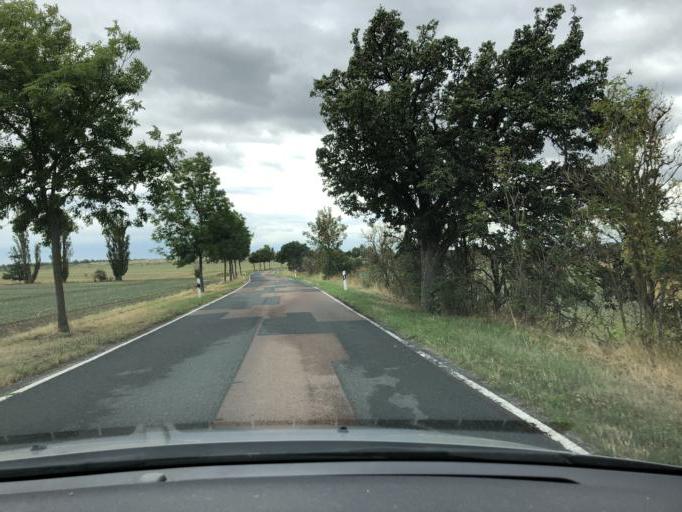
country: DE
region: Saxony-Anhalt
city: Nienburg/Saale
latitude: 51.8397
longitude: 11.7898
